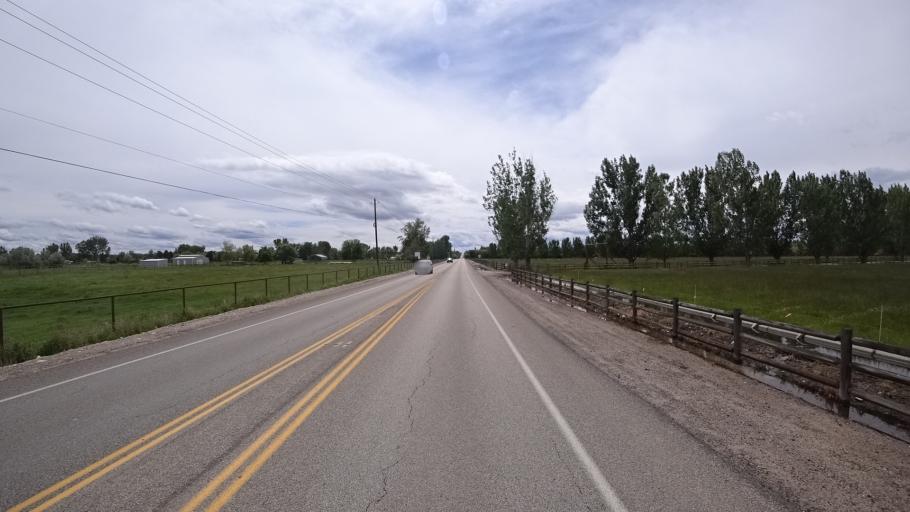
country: US
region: Idaho
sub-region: Ada County
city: Eagle
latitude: 43.6842
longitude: -116.4137
